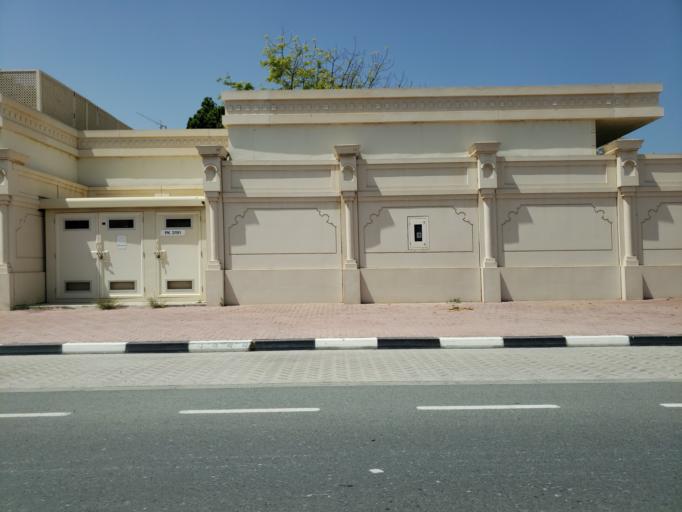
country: AE
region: Dubai
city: Dubai
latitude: 25.1167
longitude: 55.1834
